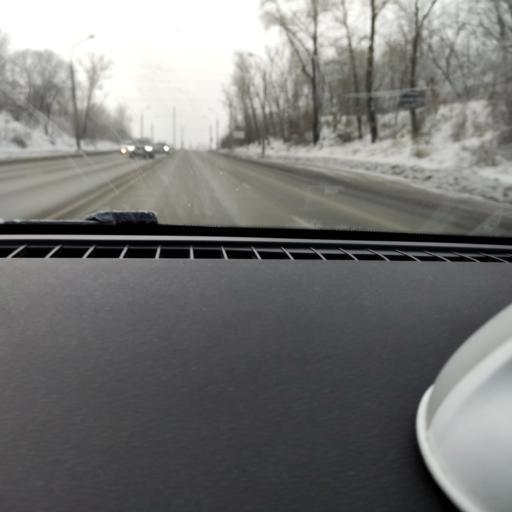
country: RU
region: Samara
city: Samara
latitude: 53.1298
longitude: 50.1735
